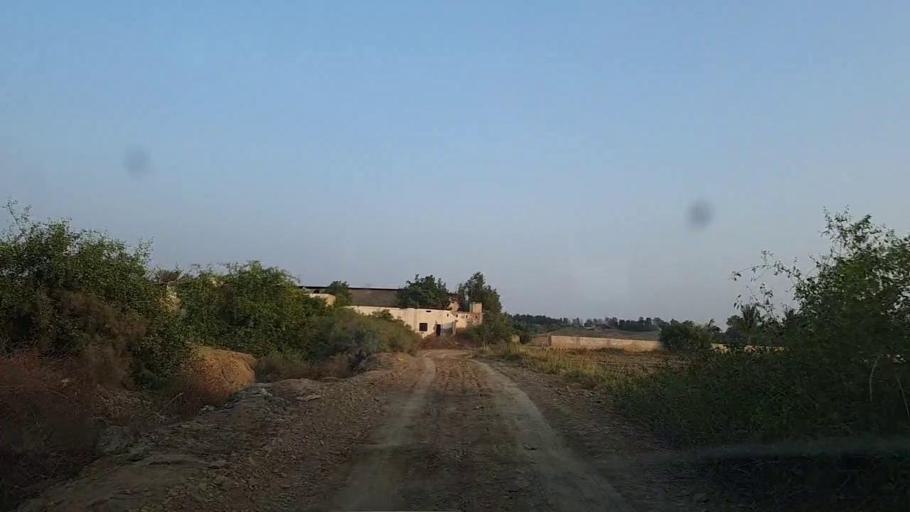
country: PK
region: Sindh
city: Mirpur Sakro
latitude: 24.6131
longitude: 67.5930
